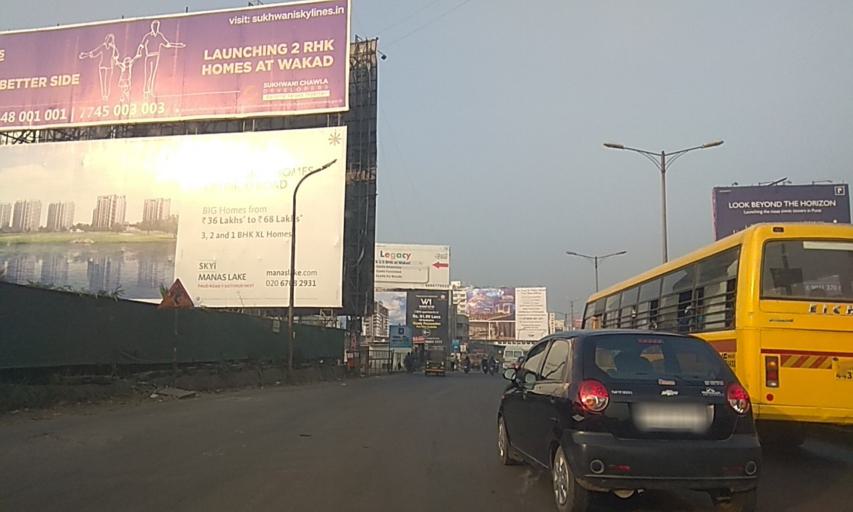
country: IN
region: Maharashtra
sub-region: Pune Division
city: Pimpri
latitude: 18.5908
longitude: 73.7519
